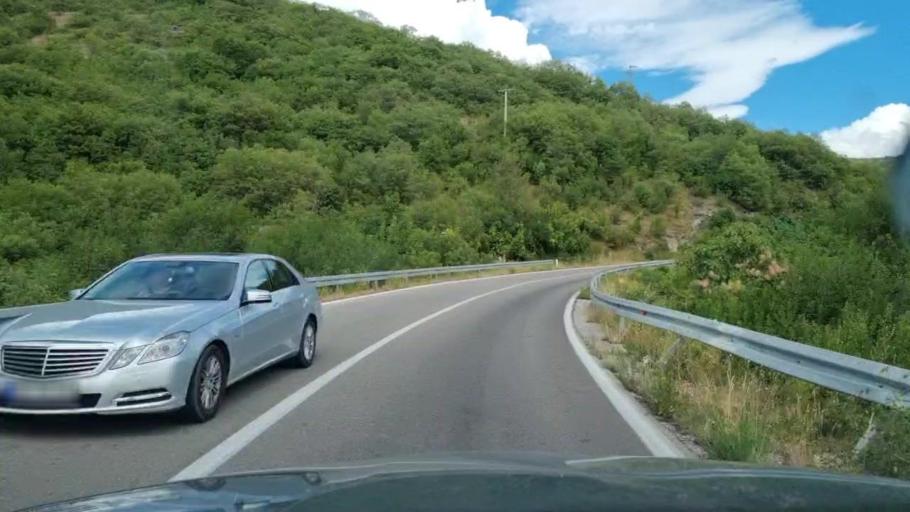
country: BA
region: Federation of Bosnia and Herzegovina
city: Blagaj
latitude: 43.2622
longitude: 17.9193
